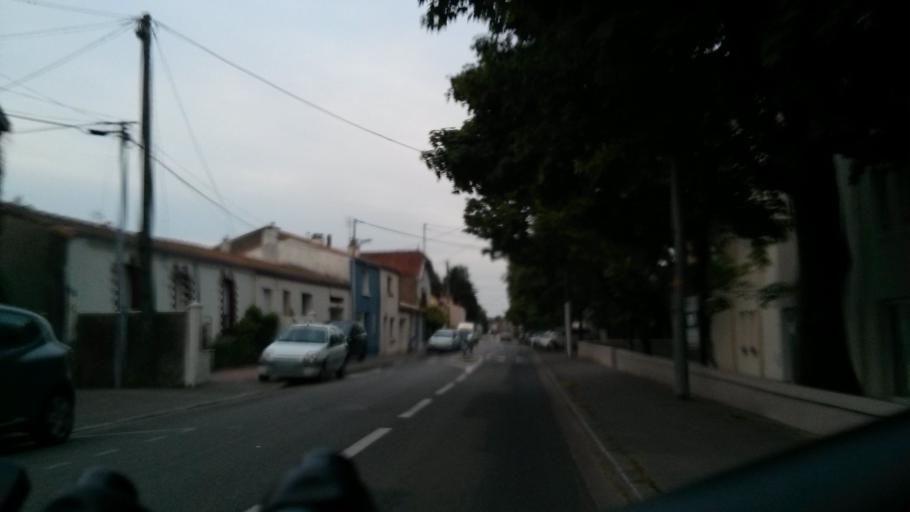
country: FR
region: Pays de la Loire
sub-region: Departement de la Loire-Atlantique
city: Reze
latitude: 47.1841
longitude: -1.5226
